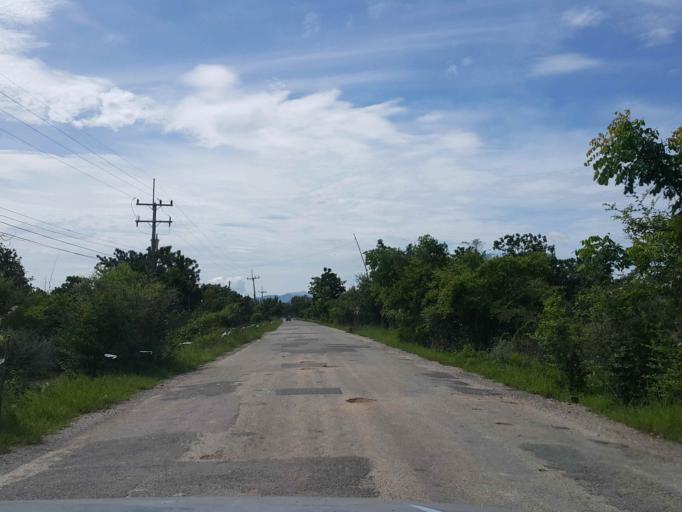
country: TH
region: Sukhothai
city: Ban Dan Lan Hoi
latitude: 17.1240
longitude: 99.5314
